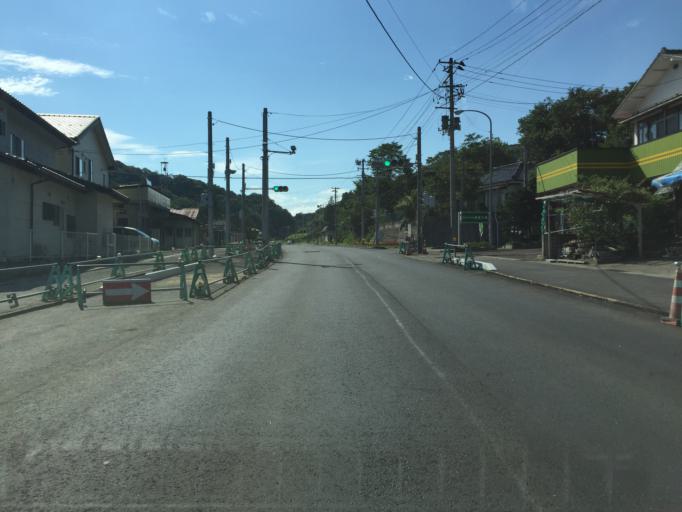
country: JP
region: Fukushima
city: Fukushima-shi
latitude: 37.6824
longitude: 140.5627
